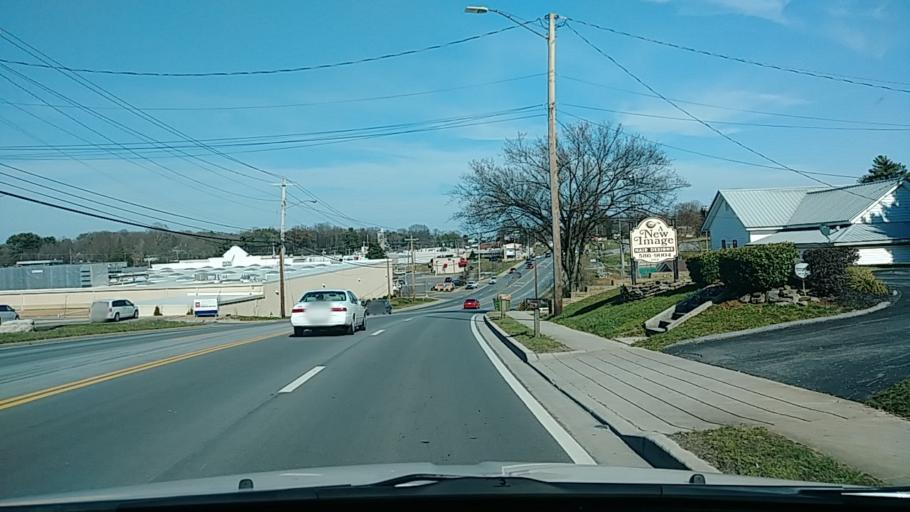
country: US
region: Tennessee
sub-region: Hamblen County
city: Morristown
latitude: 36.2163
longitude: -83.2816
